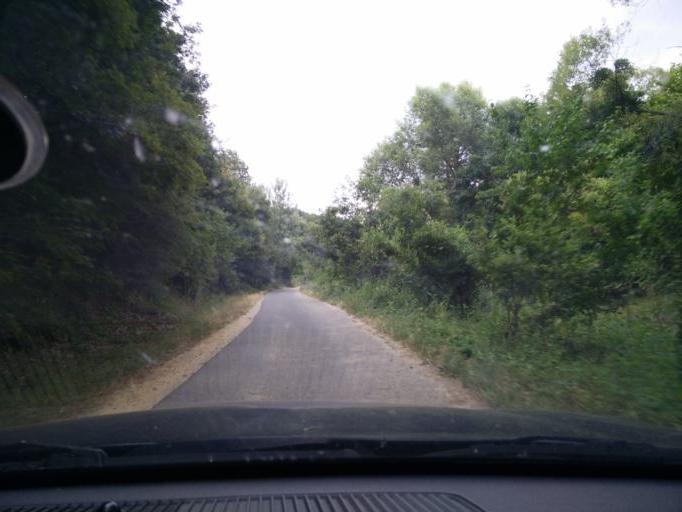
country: HU
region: Komarom-Esztergom
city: Sutto
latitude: 47.7156
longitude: 18.4535
